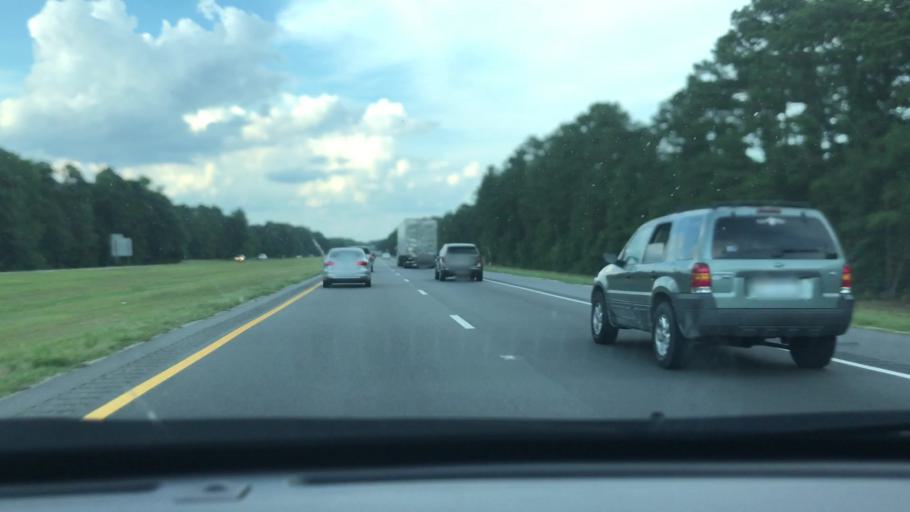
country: US
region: North Carolina
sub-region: Cumberland County
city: Hope Mills
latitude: 34.9467
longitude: -78.9069
